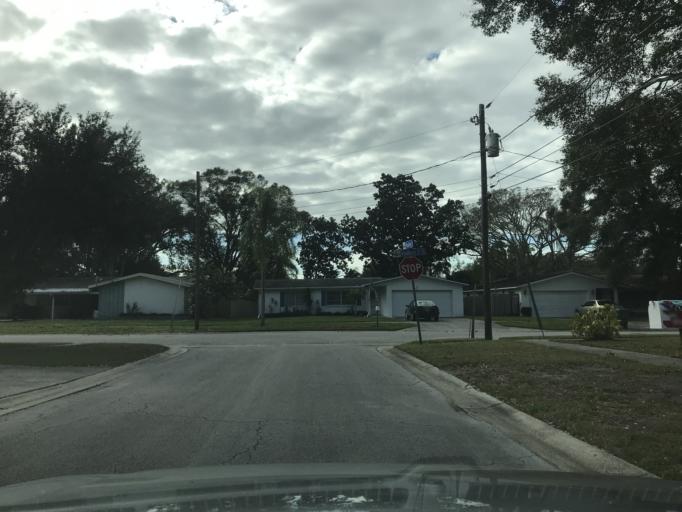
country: US
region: Florida
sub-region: Pinellas County
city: Largo
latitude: 27.9246
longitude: -82.7764
